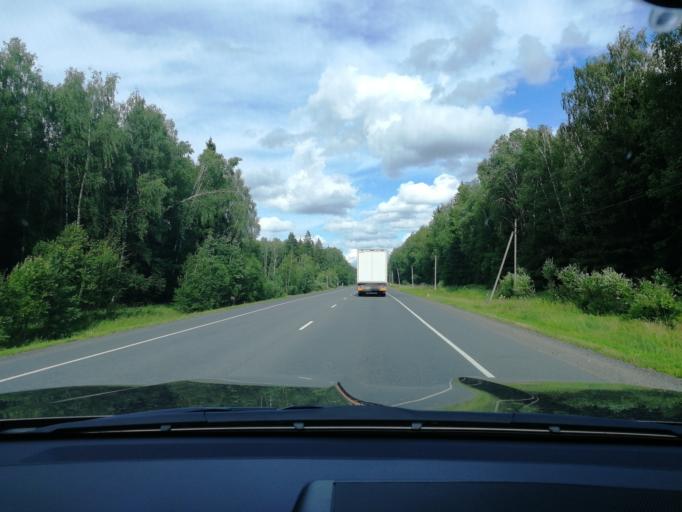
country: RU
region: Moskovskaya
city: Novyy Byt
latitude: 55.0376
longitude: 37.5975
